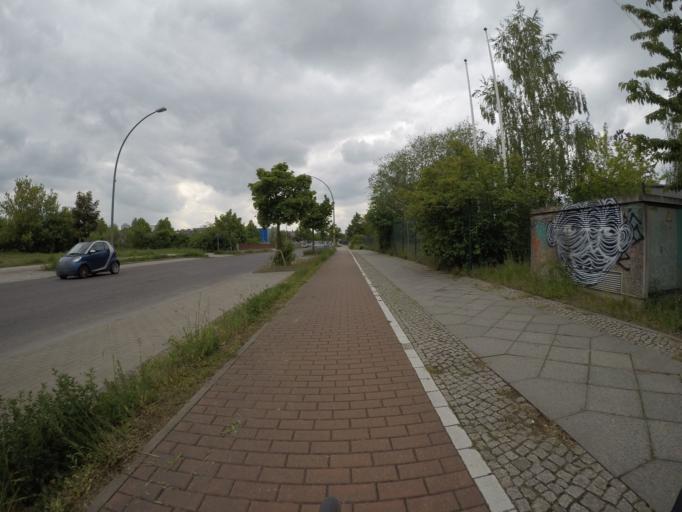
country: DE
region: Berlin
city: Falkenberg
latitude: 52.5503
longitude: 13.5372
